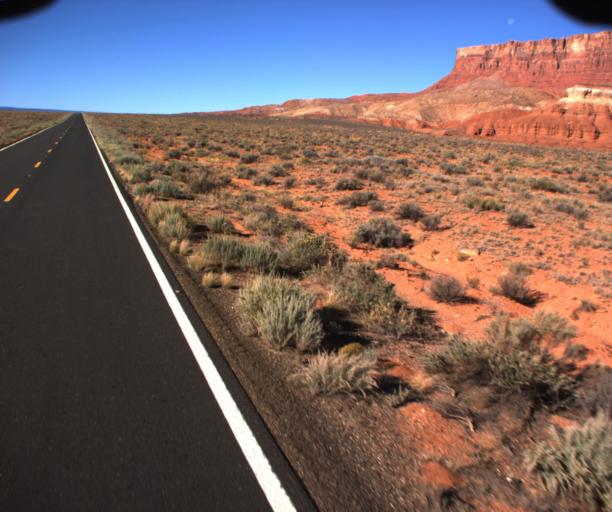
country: US
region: Arizona
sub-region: Coconino County
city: LeChee
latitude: 36.7038
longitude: -111.7892
